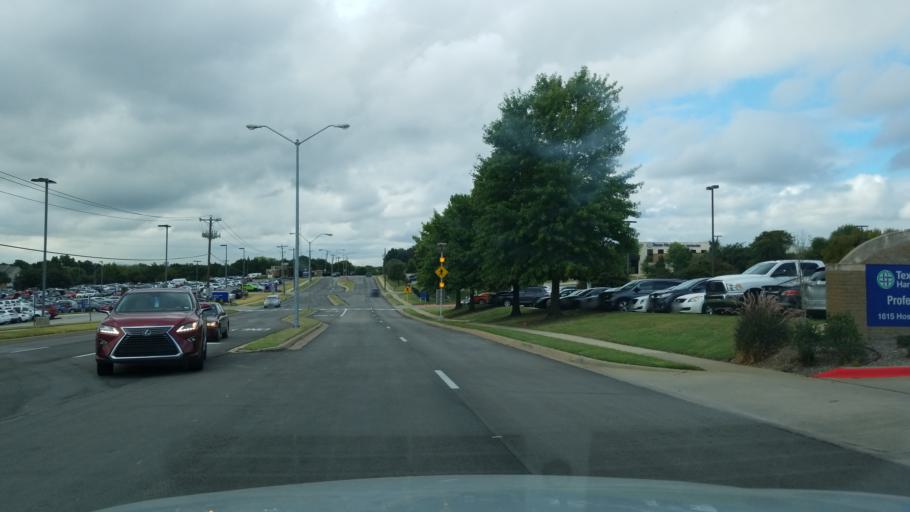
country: US
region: Texas
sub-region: Tarrant County
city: Bedford
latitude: 32.8354
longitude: -97.1254
